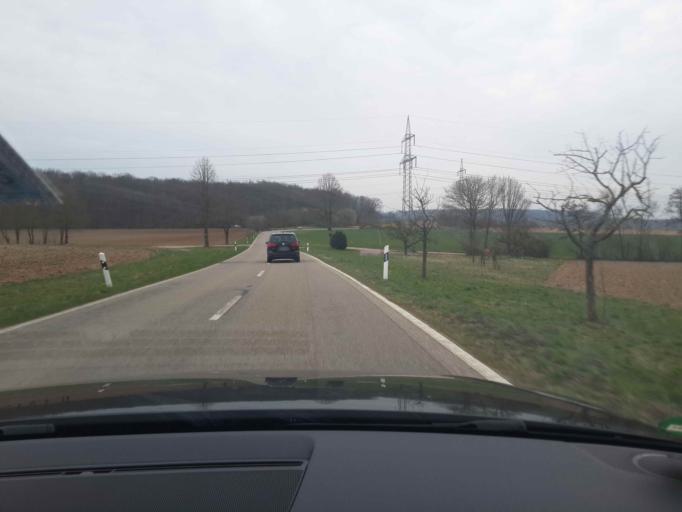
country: DE
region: Baden-Wuerttemberg
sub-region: Regierungsbezirk Stuttgart
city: Oedheim
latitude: 49.2321
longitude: 9.2677
